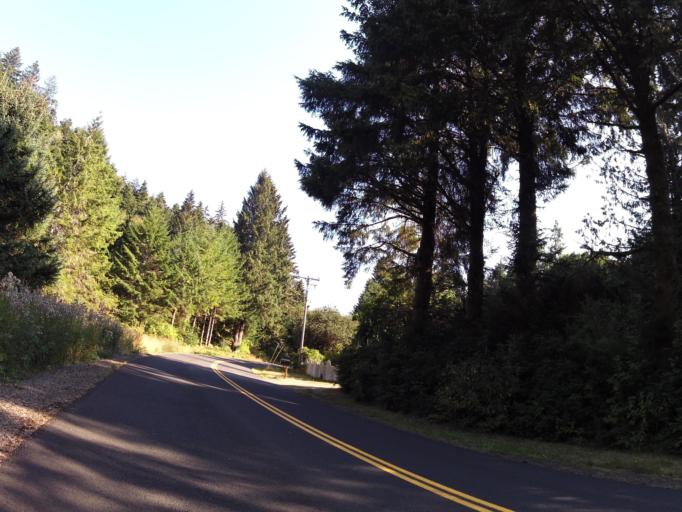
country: US
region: Oregon
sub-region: Lincoln County
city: Rose Lodge
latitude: 45.0826
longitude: -123.9457
